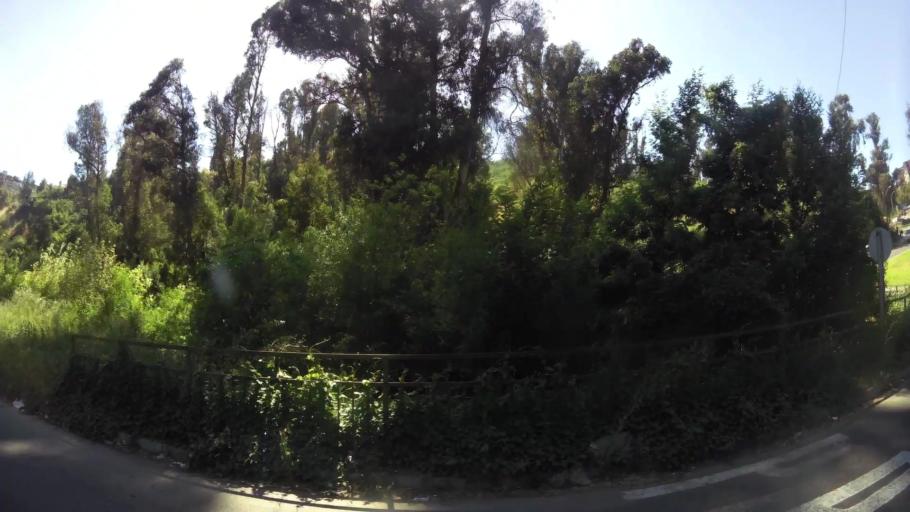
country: CL
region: Valparaiso
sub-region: Provincia de Valparaiso
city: Vina del Mar
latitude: -33.0560
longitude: -71.5838
